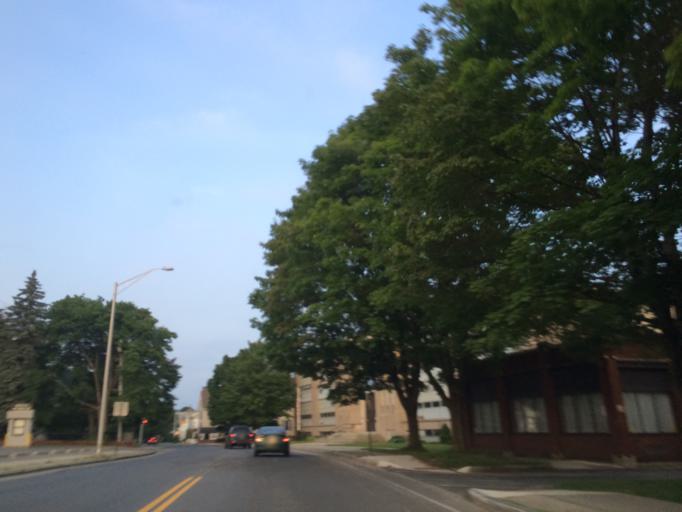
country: US
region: Massachusetts
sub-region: Berkshire County
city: Pittsfield
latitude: 42.4551
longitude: -73.2515
